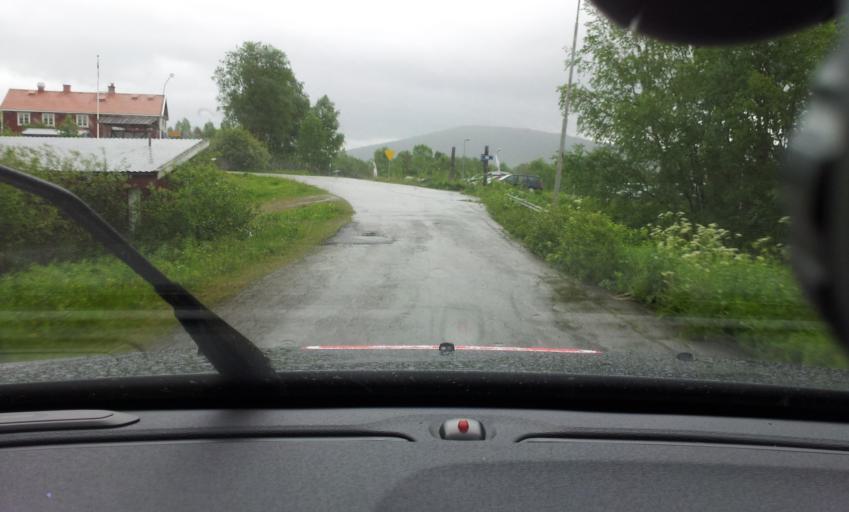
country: SE
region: Jaemtland
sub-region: Are Kommun
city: Are
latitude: 63.1480
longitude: 12.9622
